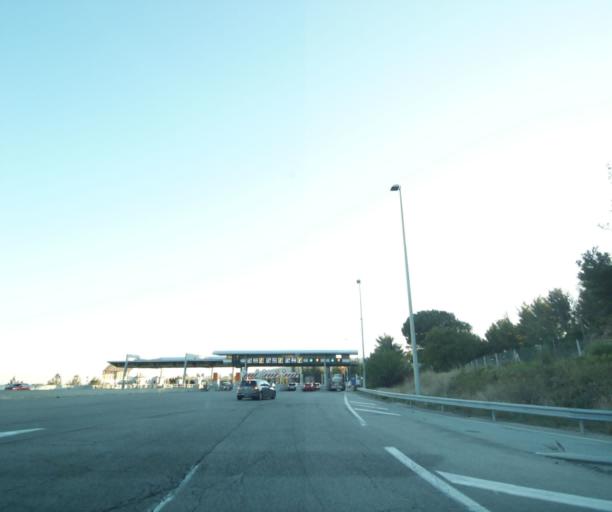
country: FR
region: Provence-Alpes-Cote d'Azur
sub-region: Departement des Bouches-du-Rhone
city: La Ciotat
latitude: 43.2030
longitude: 5.5945
